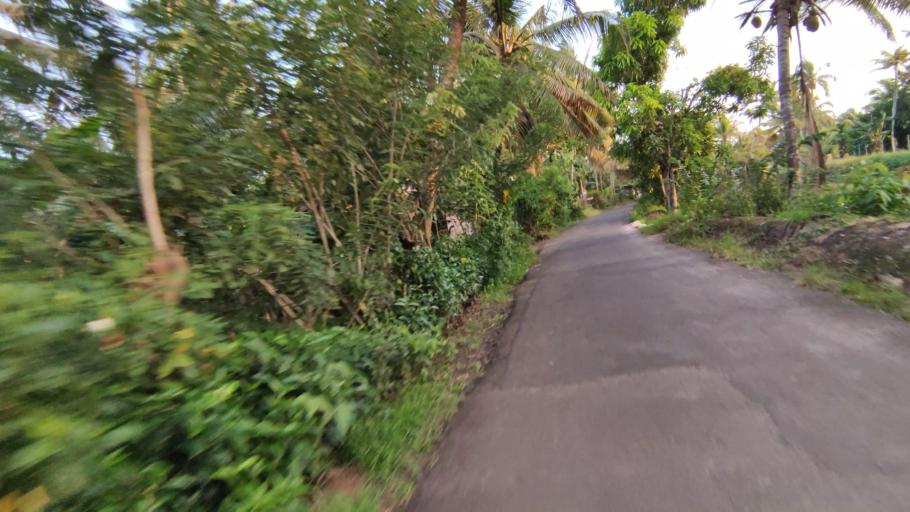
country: IN
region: Kerala
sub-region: Kottayam
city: Kottayam
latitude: 9.5821
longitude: 76.4482
